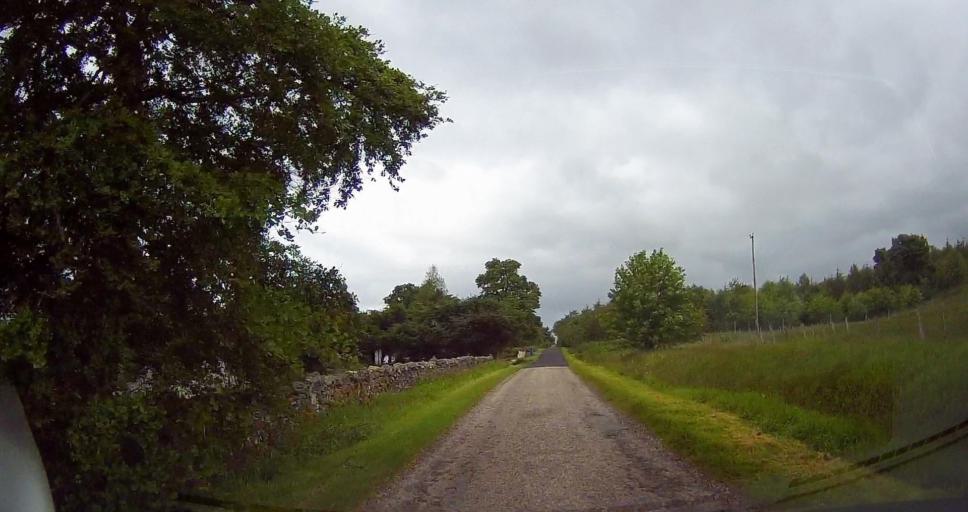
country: GB
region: Scotland
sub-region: Highland
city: Alness
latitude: 58.0804
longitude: -4.4490
